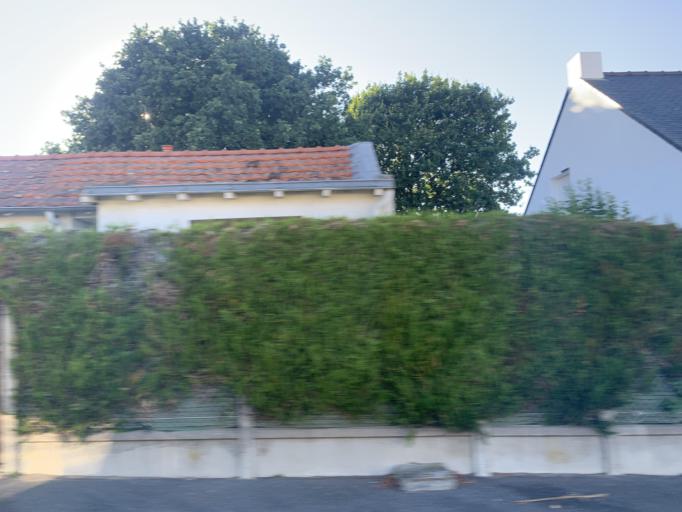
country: FR
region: Pays de la Loire
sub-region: Departement de la Loire-Atlantique
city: Pornichet
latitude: 47.2508
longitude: -2.3120
